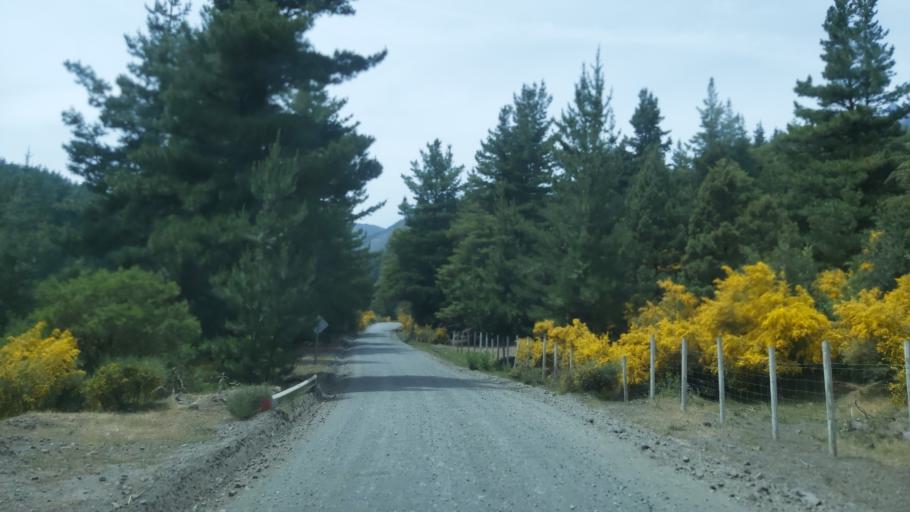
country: AR
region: Neuquen
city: Las Ovejas
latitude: -37.3943
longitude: -71.4605
